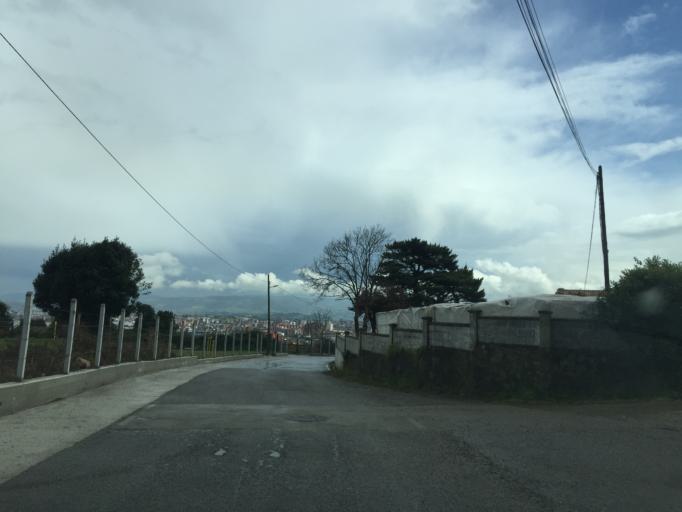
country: ES
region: Asturias
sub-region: Province of Asturias
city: Natahoyo
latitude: 43.5556
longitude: -5.7091
